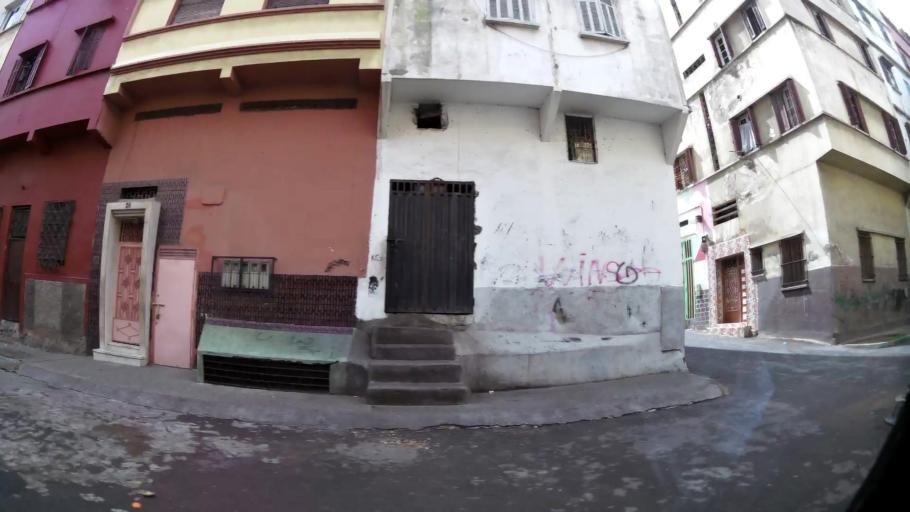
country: MA
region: Grand Casablanca
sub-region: Casablanca
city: Casablanca
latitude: 33.5648
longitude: -7.5907
